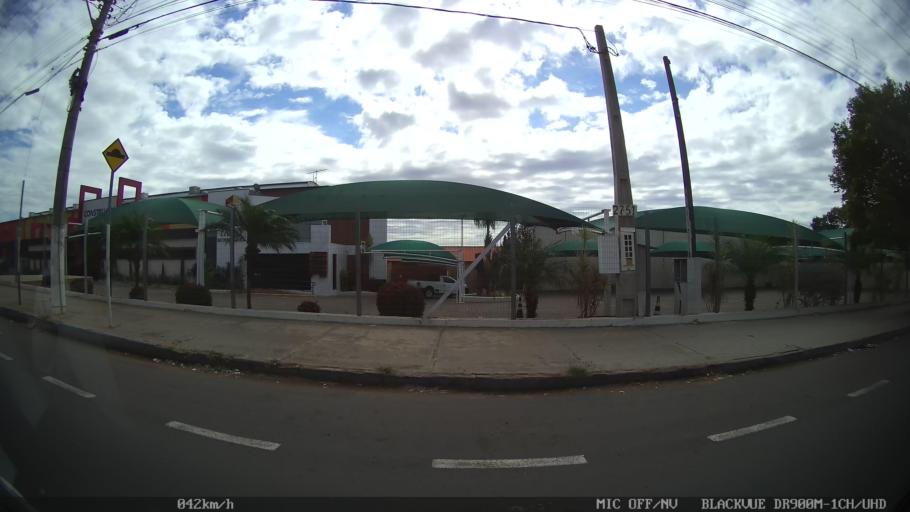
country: BR
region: Sao Paulo
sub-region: Bady Bassitt
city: Bady Bassitt
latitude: -20.8080
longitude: -49.5043
